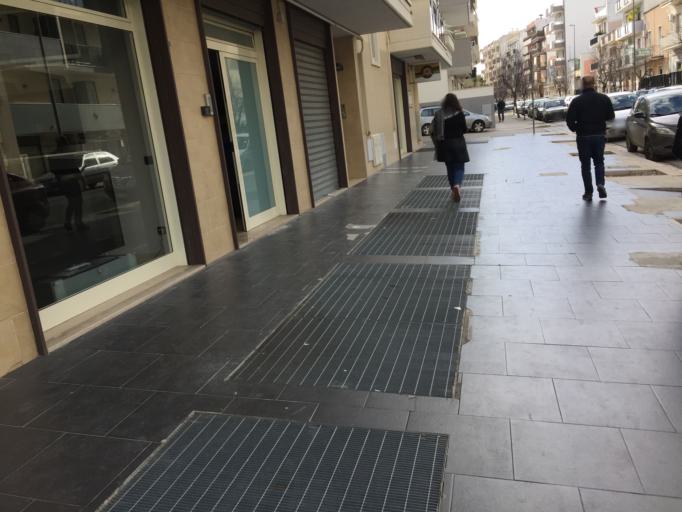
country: IT
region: Apulia
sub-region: Provincia di Barletta - Andria - Trani
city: Andria
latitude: 41.2200
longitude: 16.2997
